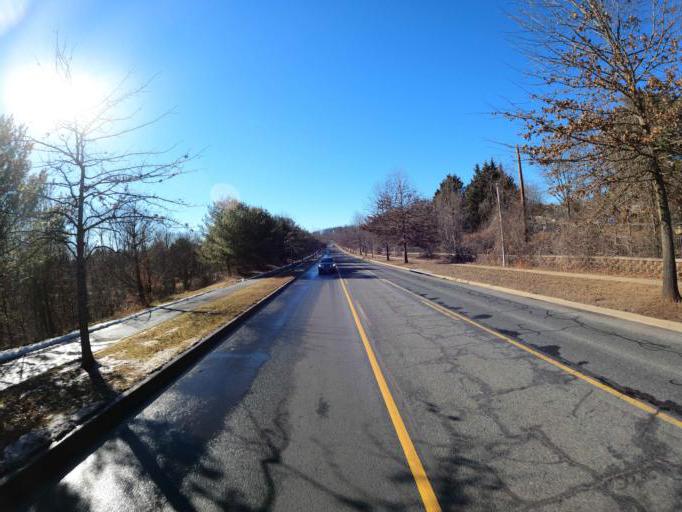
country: US
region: Maryland
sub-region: Montgomery County
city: Montgomery Village
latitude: 39.1913
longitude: -77.2290
